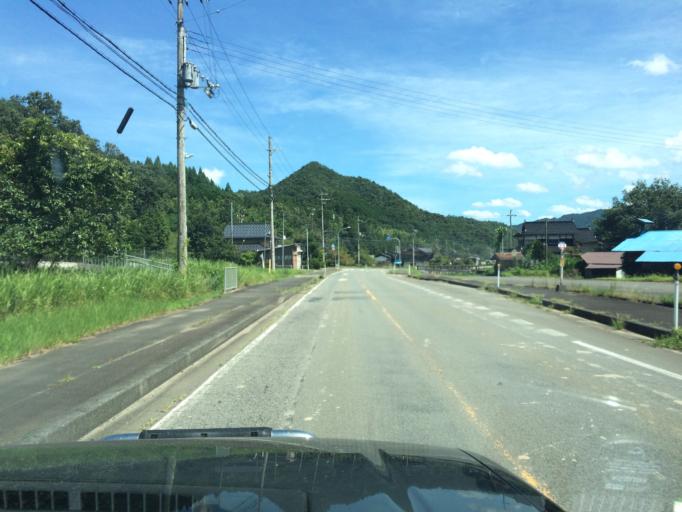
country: JP
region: Hyogo
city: Toyooka
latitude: 35.4628
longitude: 134.8317
